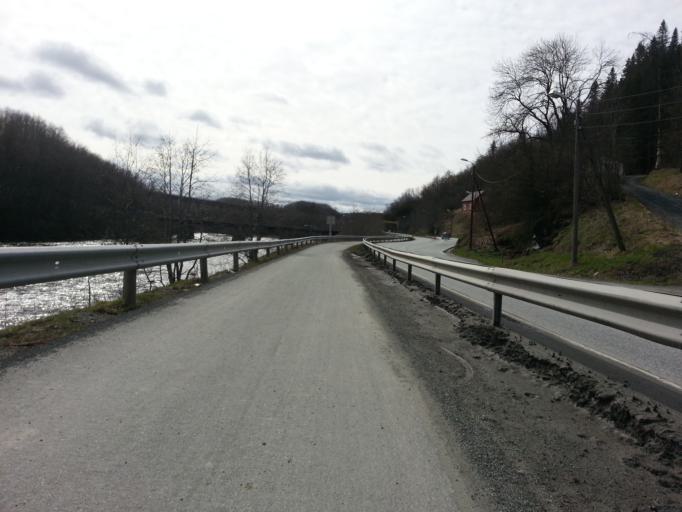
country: NO
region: Sor-Trondelag
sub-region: Trondheim
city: Trondheim
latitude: 63.3976
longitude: 10.3873
